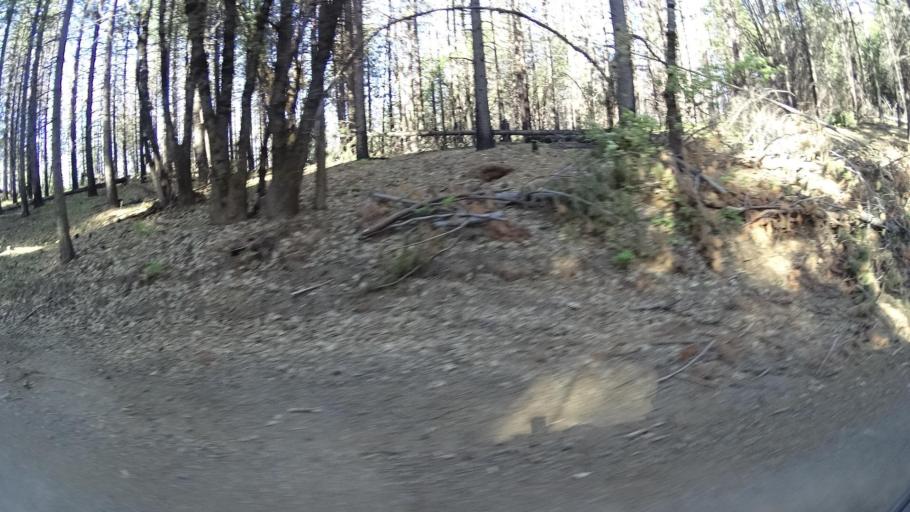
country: US
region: California
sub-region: Lake County
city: Upper Lake
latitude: 39.3514
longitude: -122.9765
